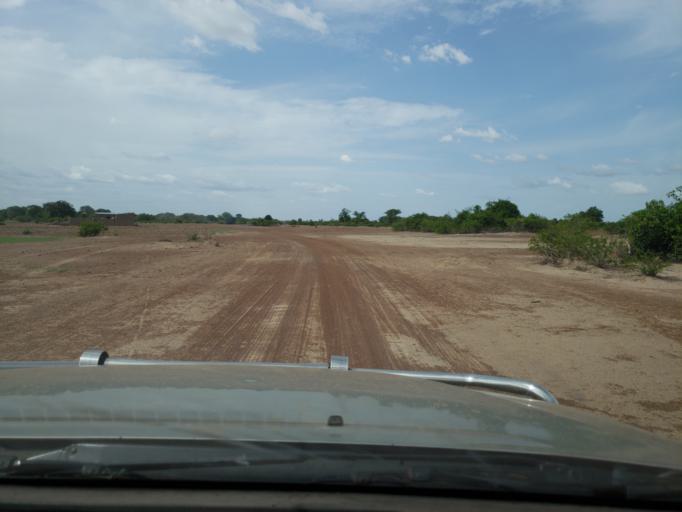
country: ML
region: Segou
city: Bla
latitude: 12.7472
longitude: -5.6348
